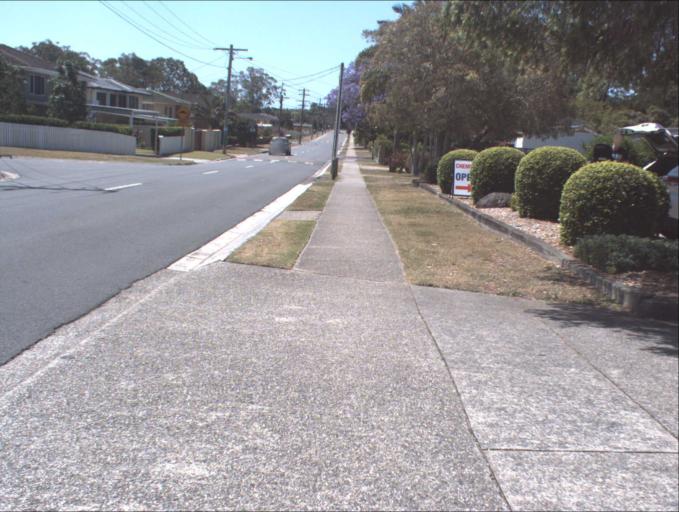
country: AU
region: Queensland
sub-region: Logan
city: Rochedale South
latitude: -27.6007
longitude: 153.1269
